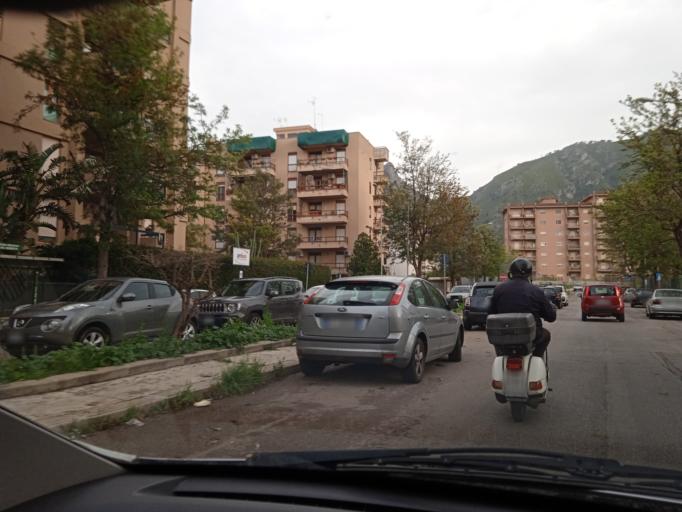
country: IT
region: Sicily
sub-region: Palermo
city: Ciaculli
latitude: 38.0853
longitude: 13.3618
